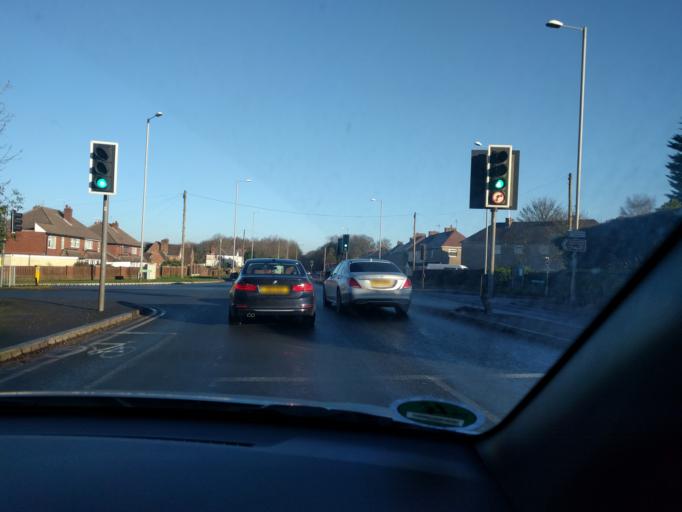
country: GB
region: England
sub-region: Staffordshire
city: Featherstone
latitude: 52.6462
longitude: -2.0846
